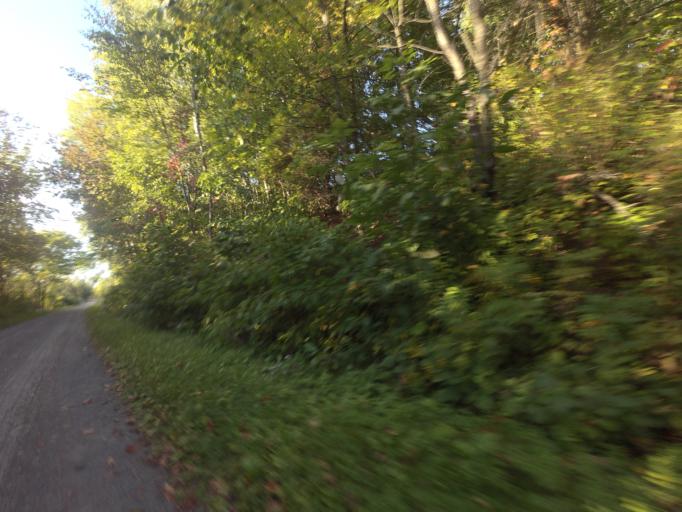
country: CA
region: Quebec
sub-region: Laurentides
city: Prevost
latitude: 45.8494
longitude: -74.0646
